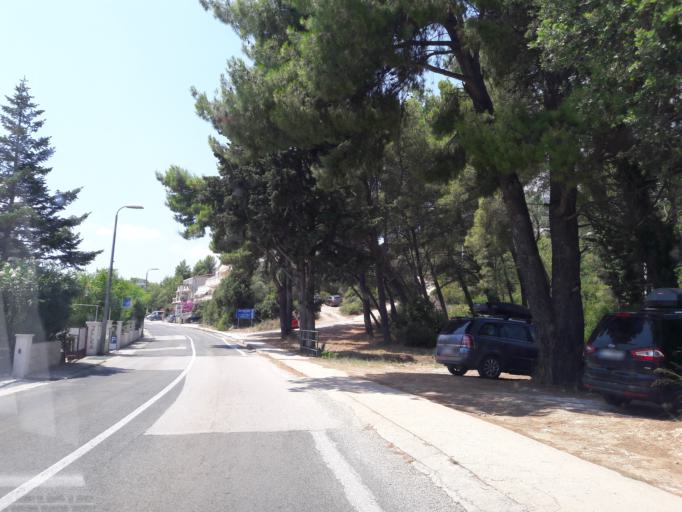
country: HR
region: Dubrovacko-Neretvanska
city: Orebic
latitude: 42.9765
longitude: 17.1720
